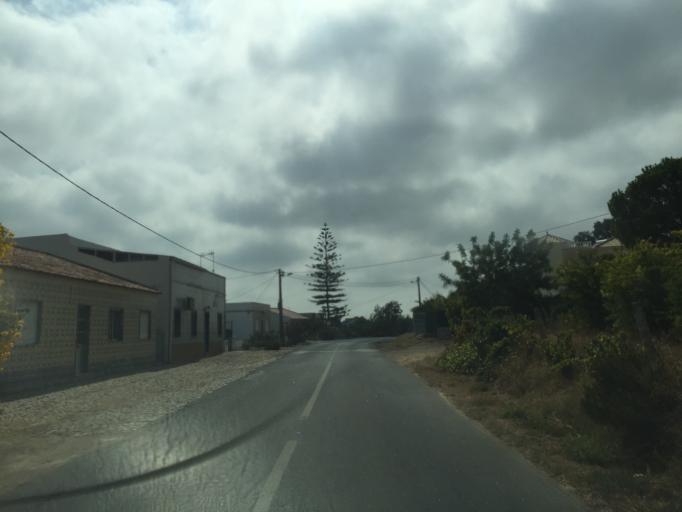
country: PT
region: Faro
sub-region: Olhao
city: Olhao
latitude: 37.0739
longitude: -7.8875
